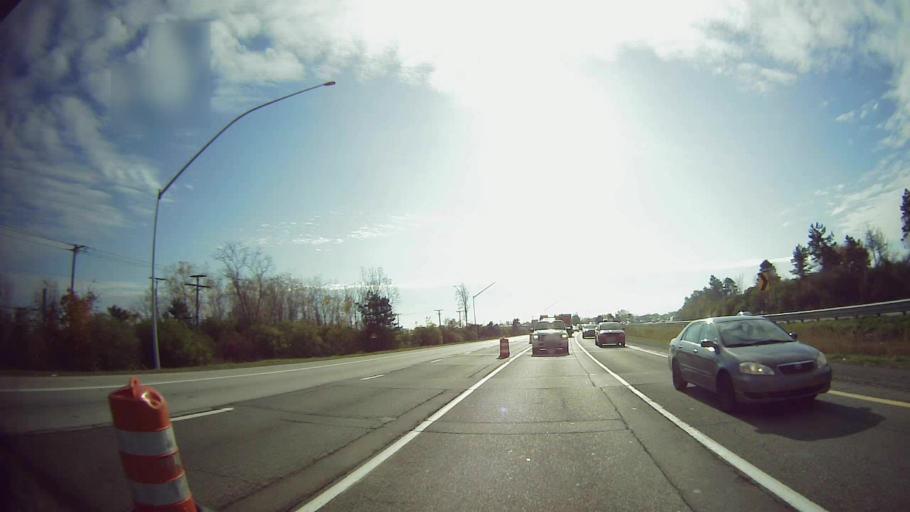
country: US
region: Michigan
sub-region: Oakland County
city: Clawson
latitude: 42.5555
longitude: -83.1180
